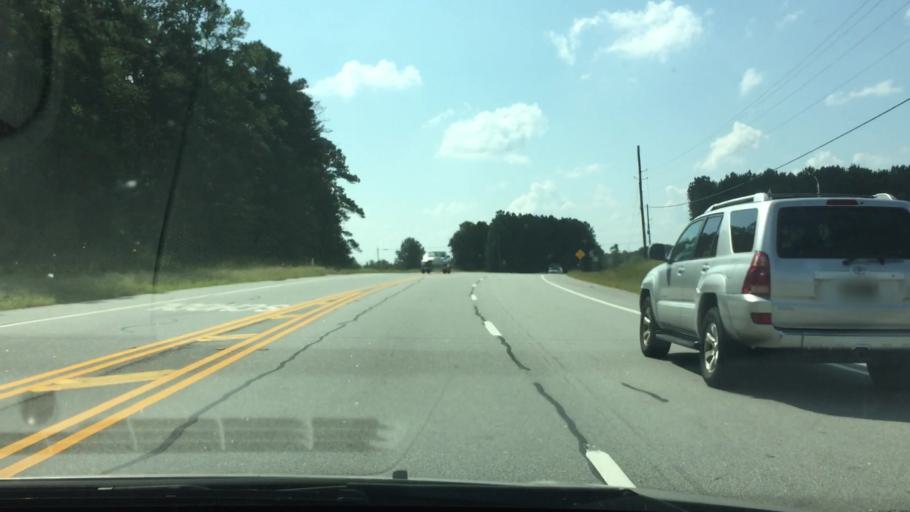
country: US
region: Georgia
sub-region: Henry County
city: Stockbridge
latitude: 33.5468
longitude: -84.1378
